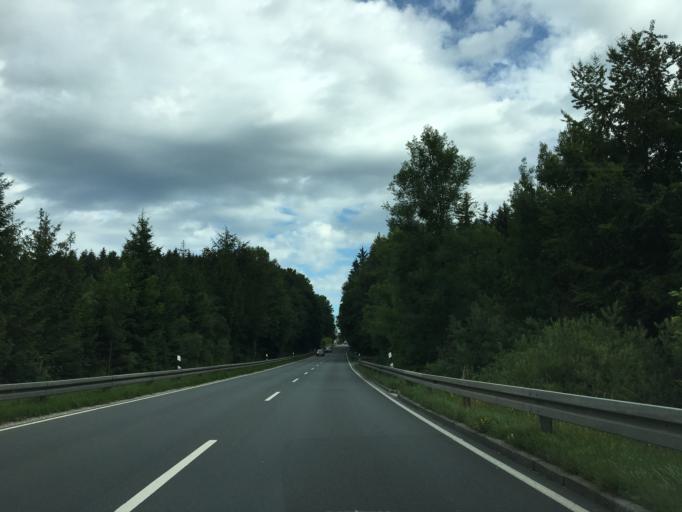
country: DE
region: Bavaria
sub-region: Upper Bavaria
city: Otterfing
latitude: 47.8939
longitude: 11.6778
